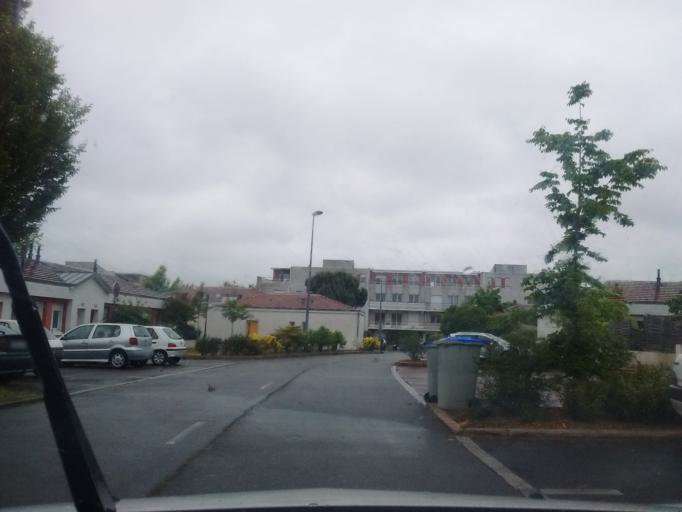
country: FR
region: Pays de la Loire
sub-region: Departement de la Loire-Atlantique
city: Nantes
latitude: 47.2524
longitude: -1.5334
